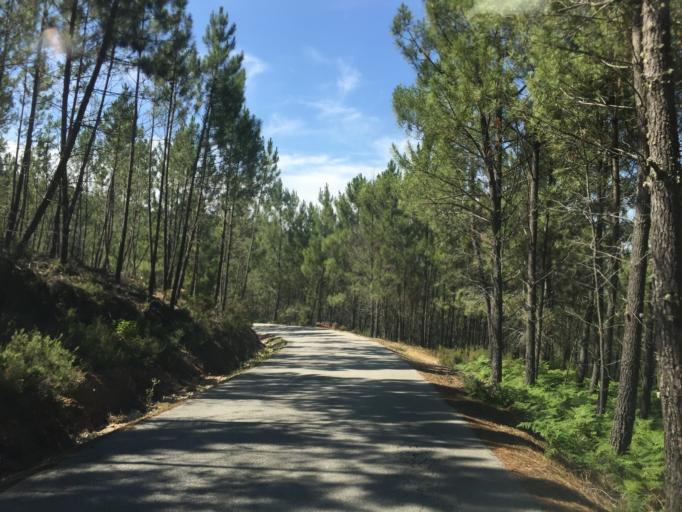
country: PT
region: Castelo Branco
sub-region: Oleiros
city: Oleiros
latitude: 39.9803
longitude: -7.8470
